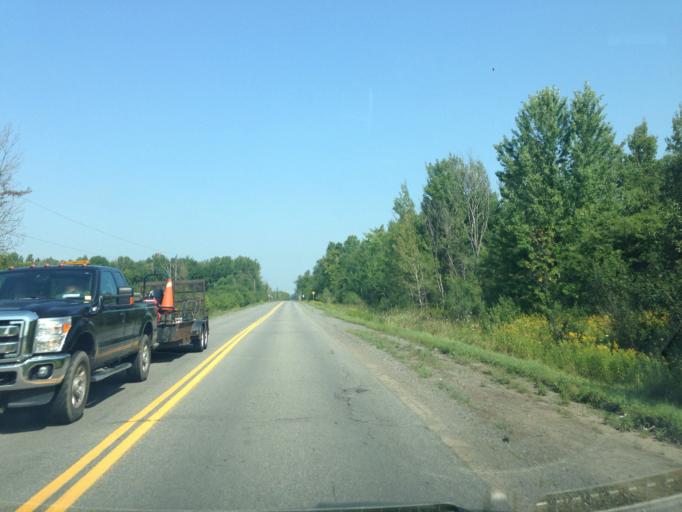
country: CA
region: Ontario
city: Ottawa
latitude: 45.3891
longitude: -75.5500
